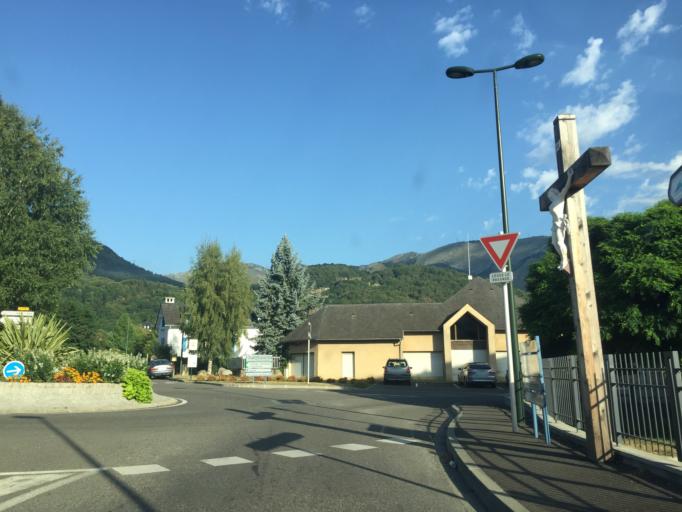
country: FR
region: Midi-Pyrenees
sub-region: Departement des Hautes-Pyrenees
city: Argeles-Gazost
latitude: 43.0067
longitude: -0.0924
